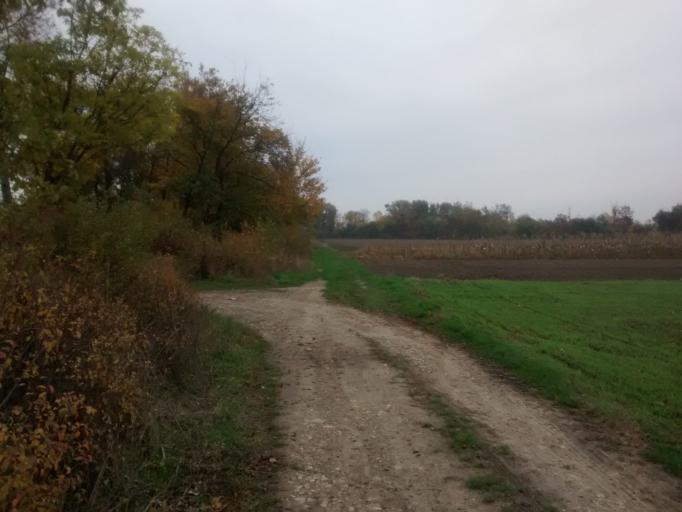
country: AT
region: Lower Austria
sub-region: Politischer Bezirk Baden
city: Trumau
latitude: 48.0108
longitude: 16.3634
